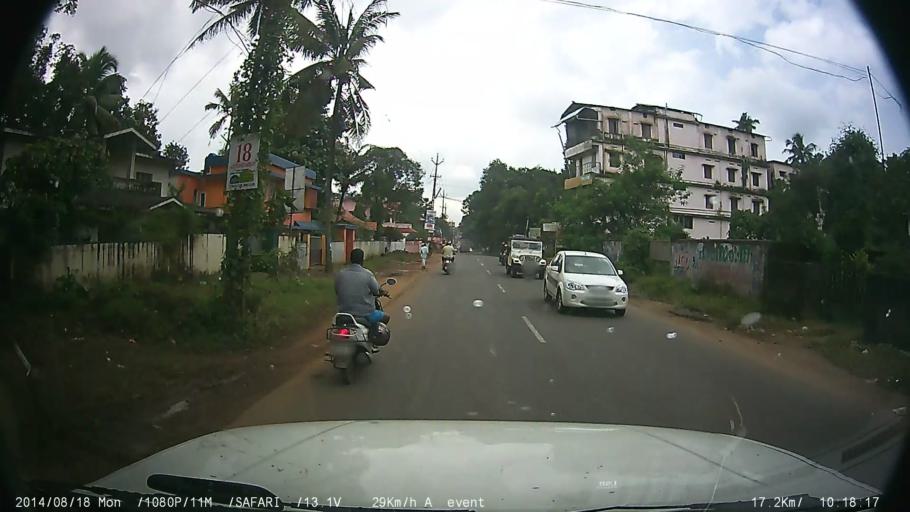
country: IN
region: Kerala
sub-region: Kottayam
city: Palackattumala
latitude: 9.6784
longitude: 76.5577
